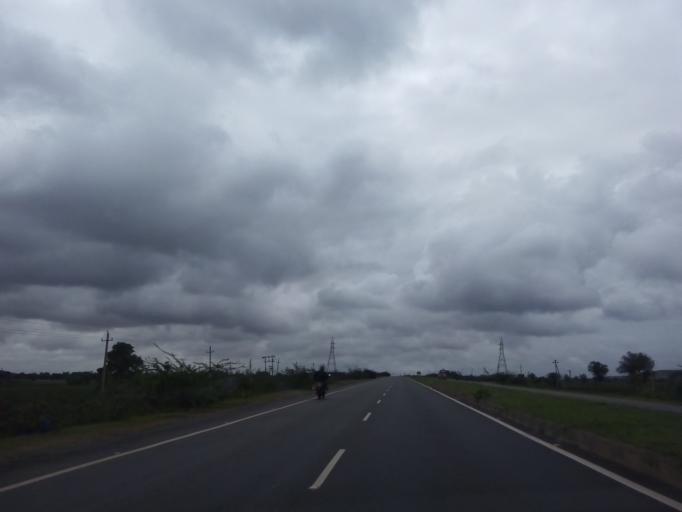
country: IN
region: Karnataka
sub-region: Haveri
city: Haveri
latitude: 14.7741
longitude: 75.4071
